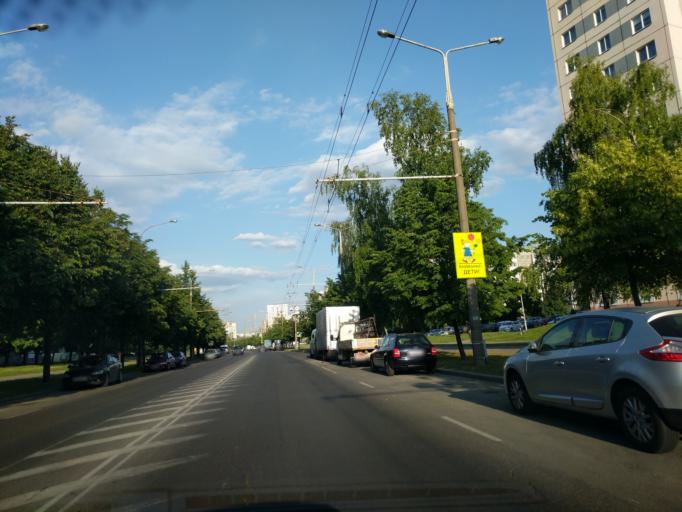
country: BY
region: Minsk
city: Malinovka
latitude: 53.8499
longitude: 27.4595
